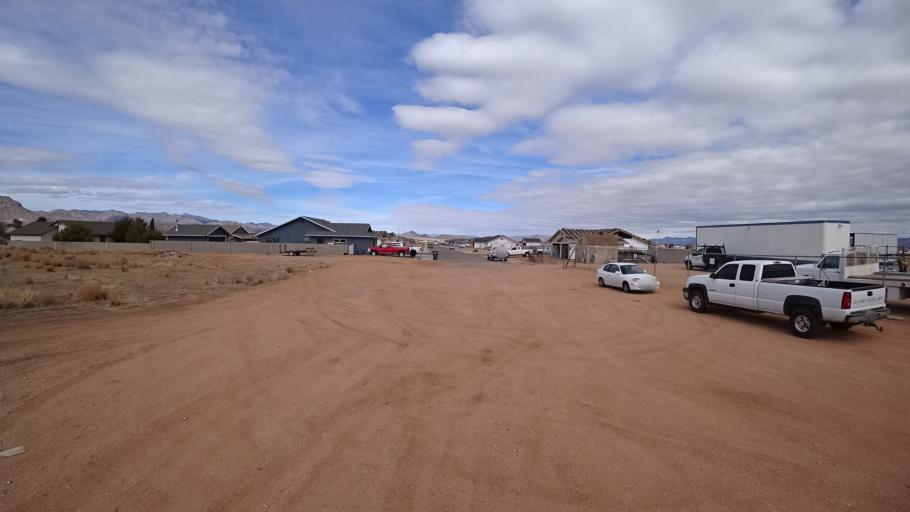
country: US
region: Arizona
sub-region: Mohave County
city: New Kingman-Butler
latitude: 35.2355
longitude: -113.9989
